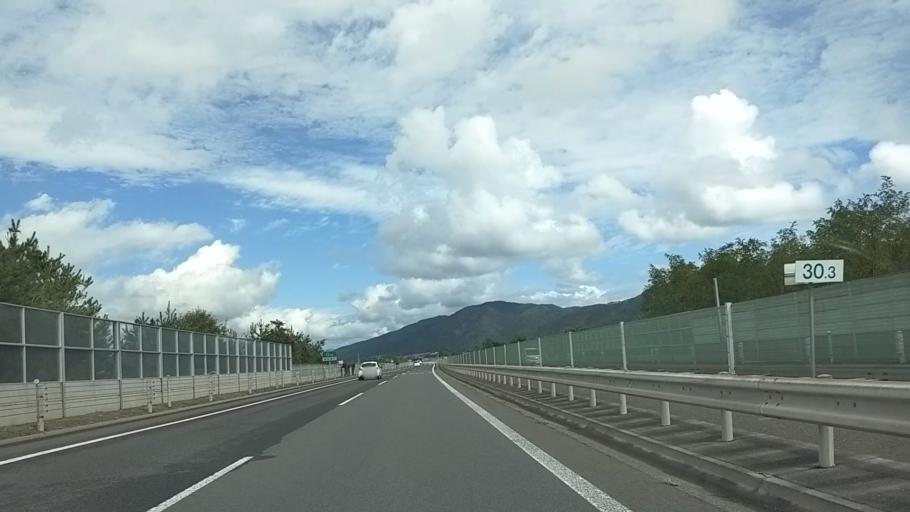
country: JP
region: Nagano
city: Toyoshina
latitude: 36.2737
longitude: 137.9307
